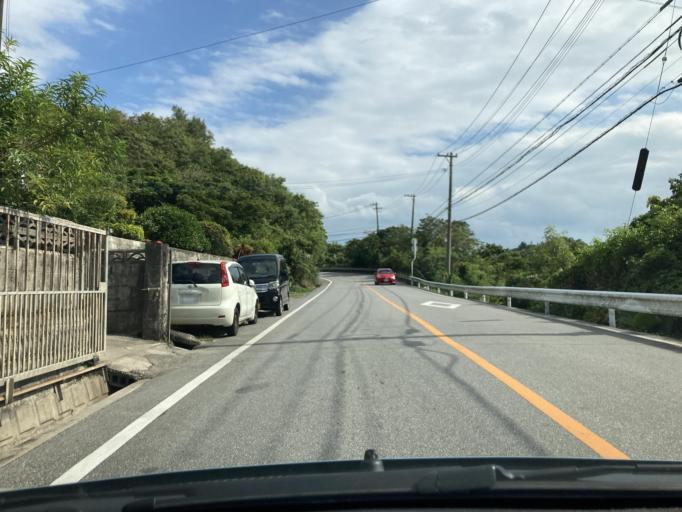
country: JP
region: Okinawa
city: Ginowan
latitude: 26.2699
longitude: 127.7821
